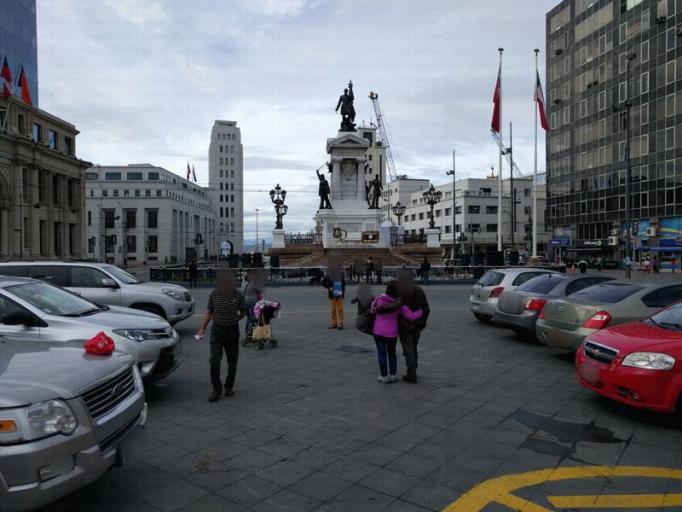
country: CL
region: Valparaiso
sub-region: Provincia de Valparaiso
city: Valparaiso
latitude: -33.0386
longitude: -71.6289
